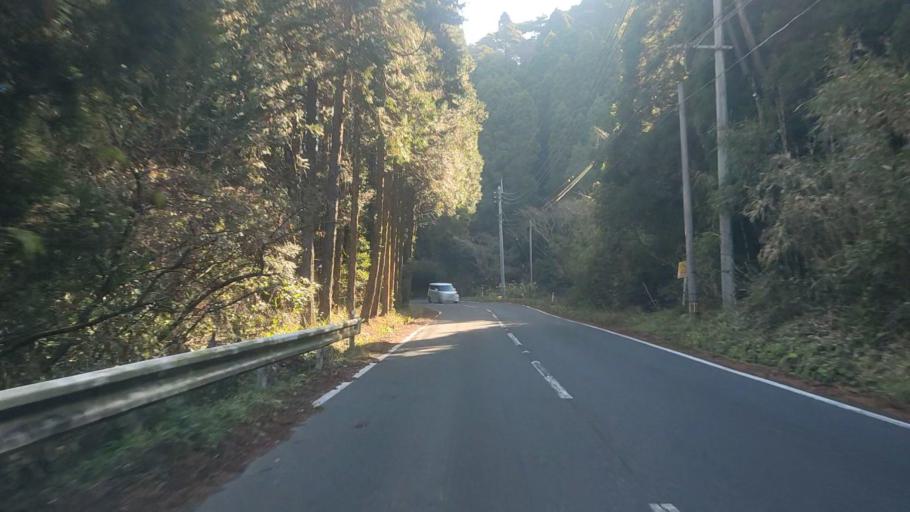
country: JP
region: Kagoshima
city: Kokubu-matsuki
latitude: 31.6697
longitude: 130.8362
